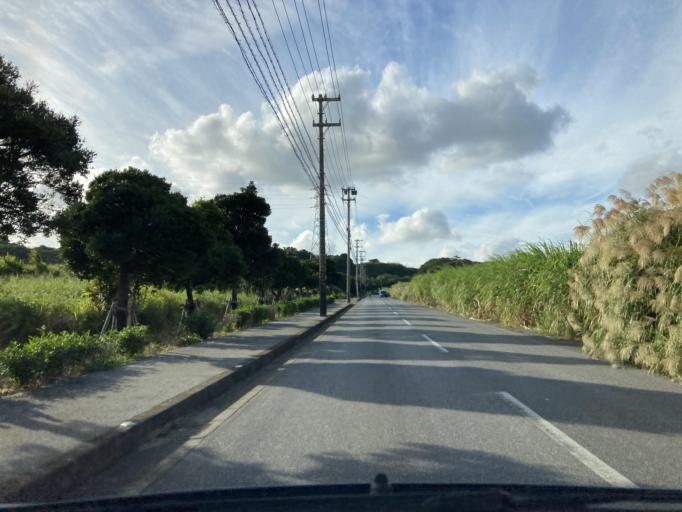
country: JP
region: Okinawa
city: Itoman
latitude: 26.1353
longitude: 127.7489
